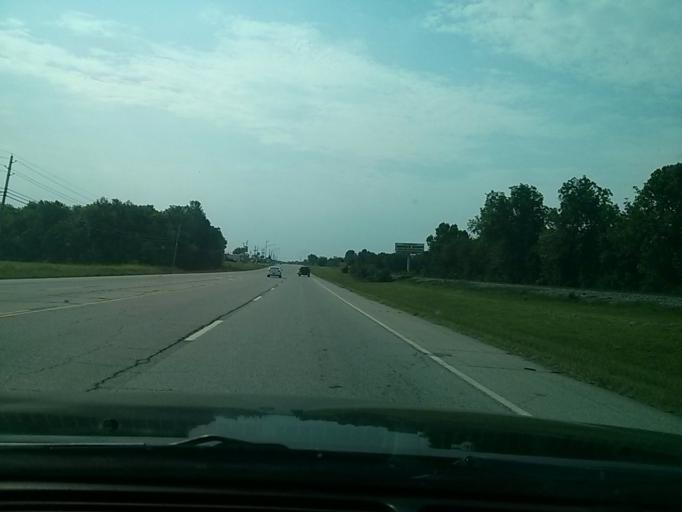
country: US
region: Oklahoma
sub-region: Wagoner County
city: Coweta
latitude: 35.9722
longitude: -95.6606
